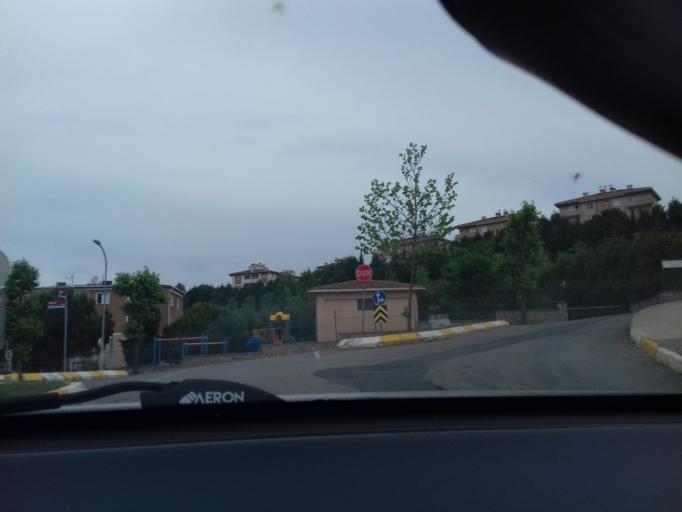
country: TR
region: Istanbul
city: Sultanbeyli
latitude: 40.9332
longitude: 29.2975
